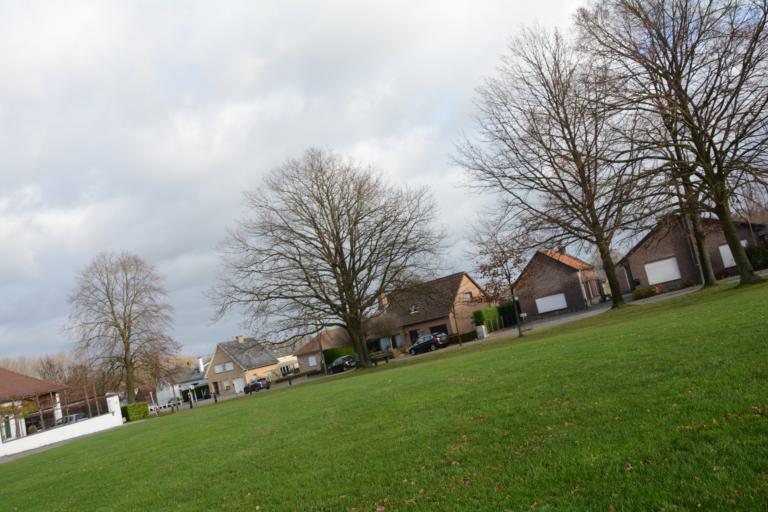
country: BE
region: Flanders
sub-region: Provincie Vlaams-Brabant
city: Opwijk
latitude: 50.9416
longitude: 4.1753
